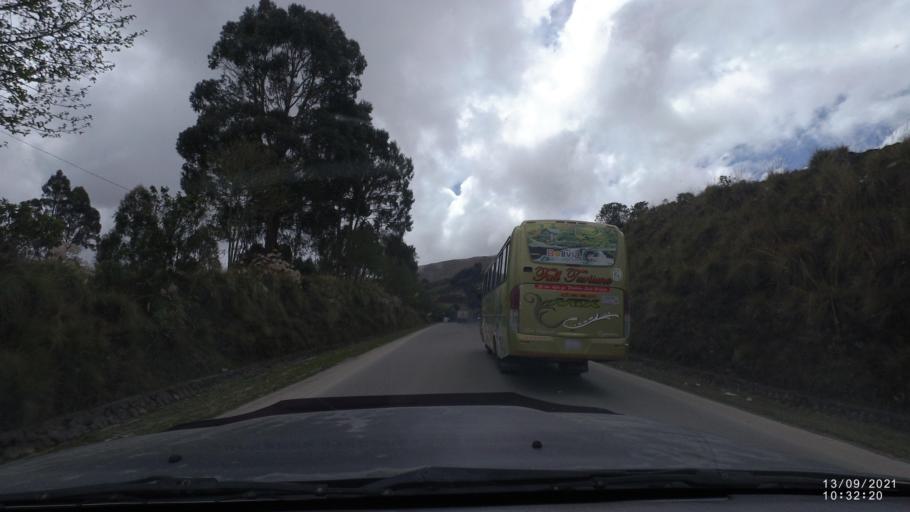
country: BO
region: Cochabamba
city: Colomi
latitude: -17.2492
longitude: -65.8930
